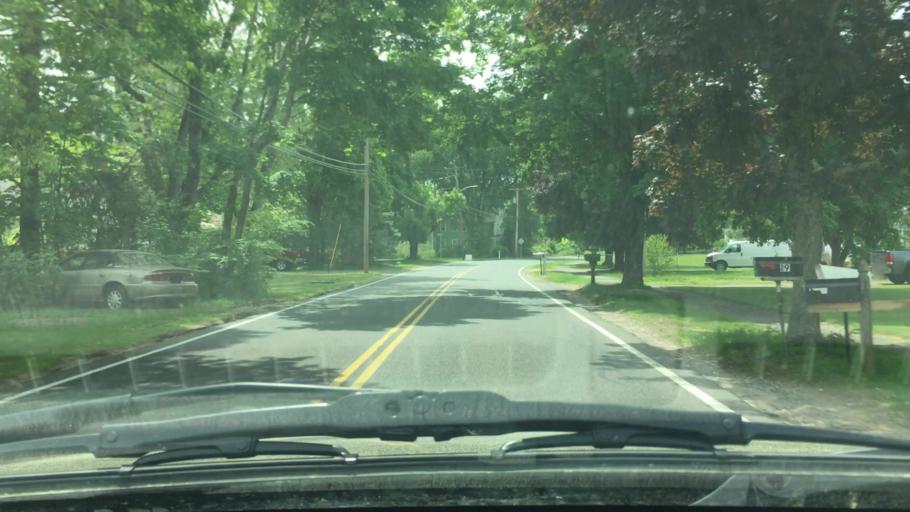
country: US
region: Massachusetts
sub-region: Hampshire County
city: Belchertown
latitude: 42.2703
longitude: -72.3977
